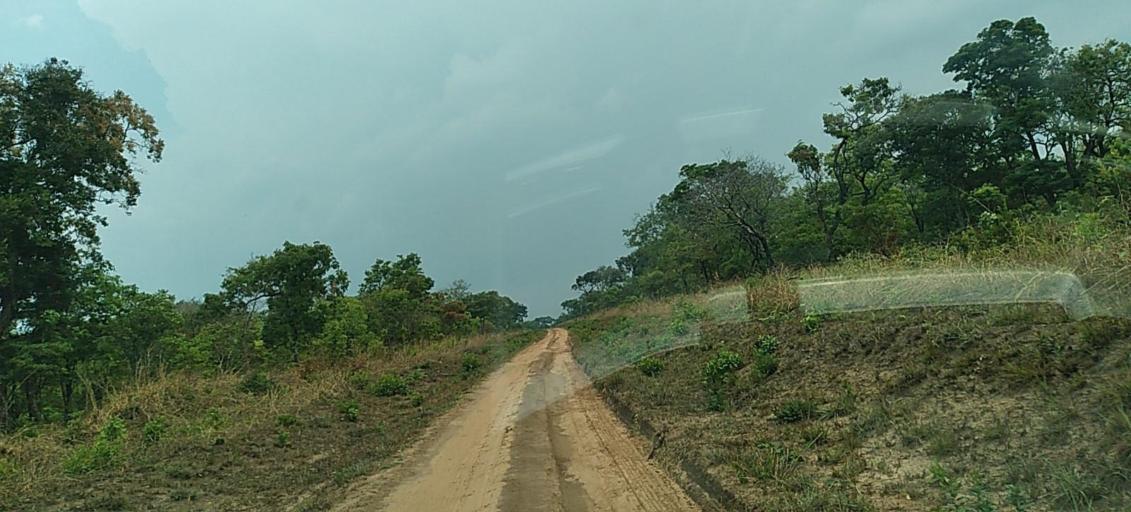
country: ZM
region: North-Western
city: Mwinilunga
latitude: -11.4362
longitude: 24.5942
